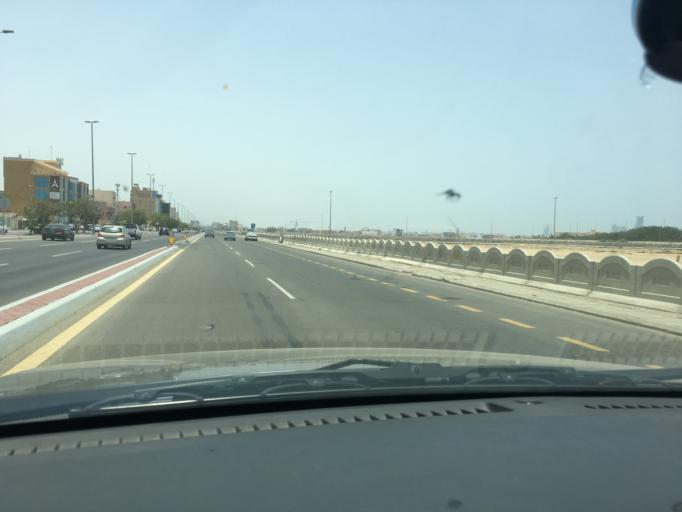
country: SA
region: Makkah
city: Jeddah
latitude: 21.6502
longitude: 39.1262
